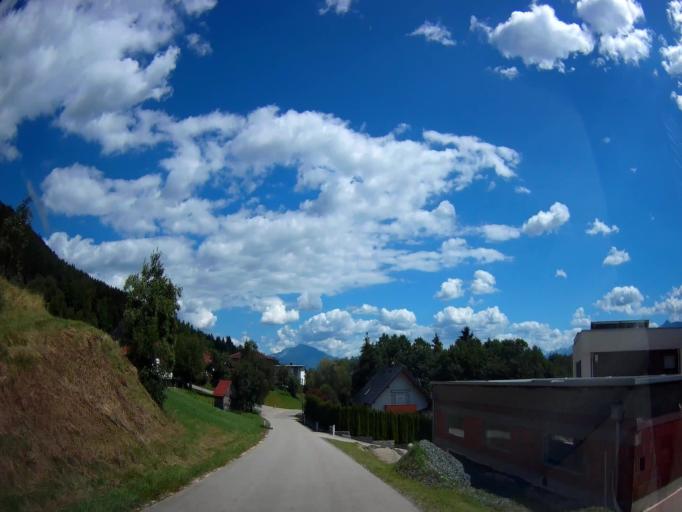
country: AT
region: Carinthia
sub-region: Politischer Bezirk Klagenfurt Land
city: Poggersdorf
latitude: 46.6640
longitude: 14.5354
